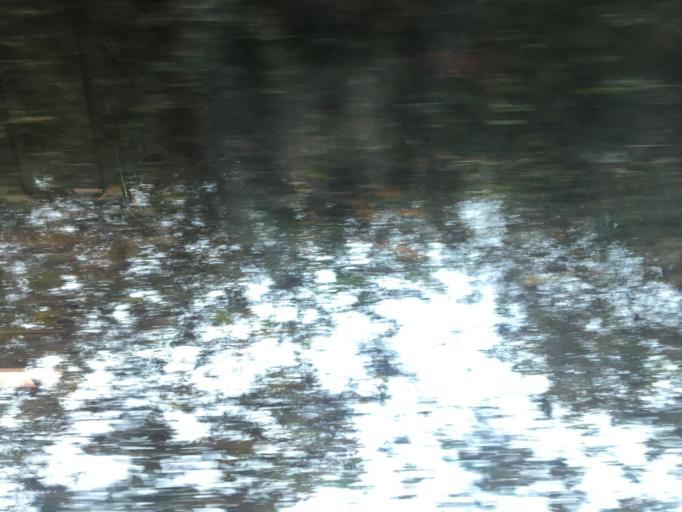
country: JP
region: Ibaraki
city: Iwase
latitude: 36.3427
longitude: 140.0678
